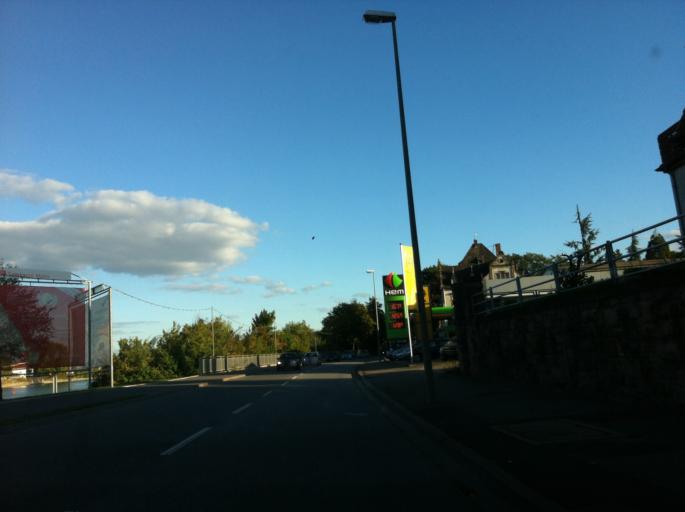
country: DE
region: Rheinland-Pfalz
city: Nierstein
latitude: 49.8691
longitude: 8.3478
